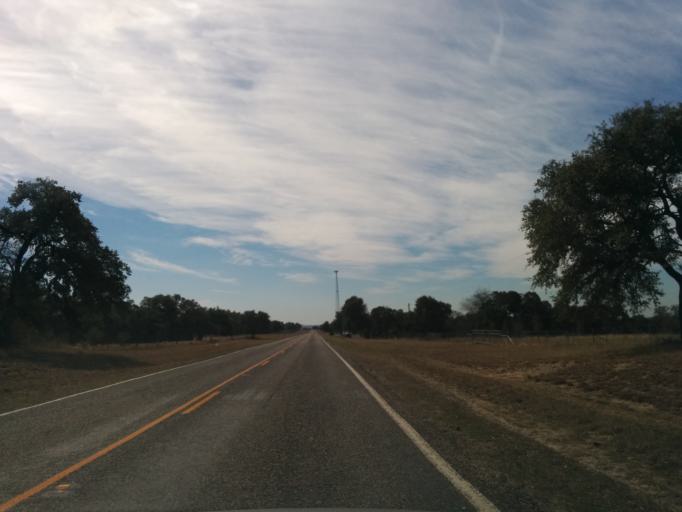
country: US
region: Texas
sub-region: Bexar County
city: Fair Oaks Ranch
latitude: 29.9367
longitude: -98.5676
